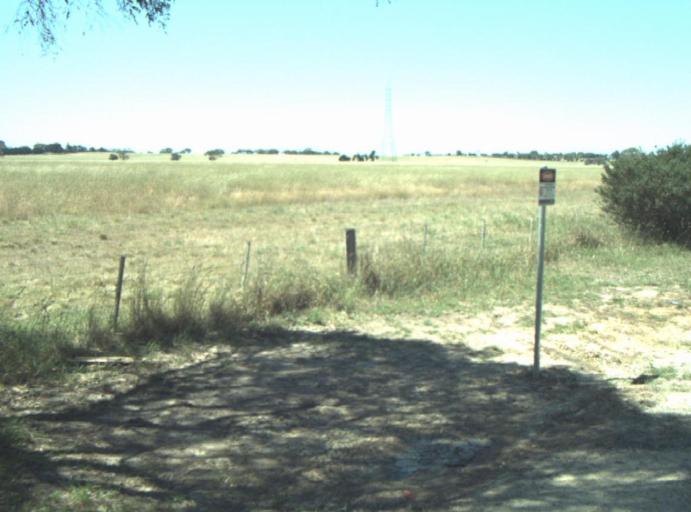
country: AU
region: Victoria
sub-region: Greater Geelong
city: Breakwater
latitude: -38.2397
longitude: 144.3529
